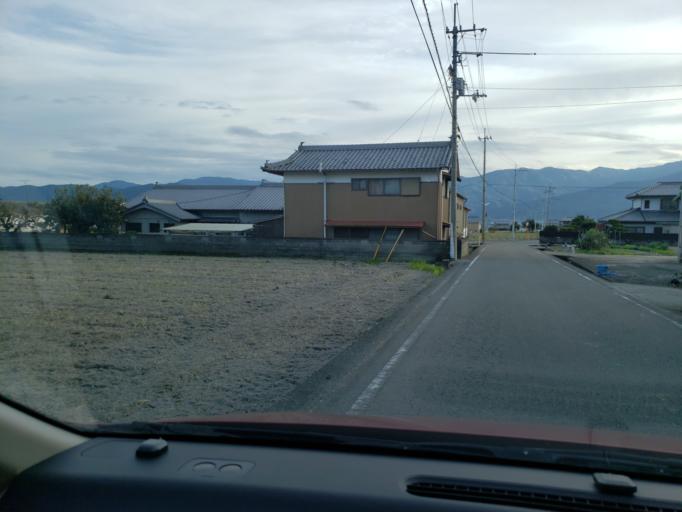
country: JP
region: Tokushima
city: Wakimachi
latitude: 34.0883
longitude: 134.2268
